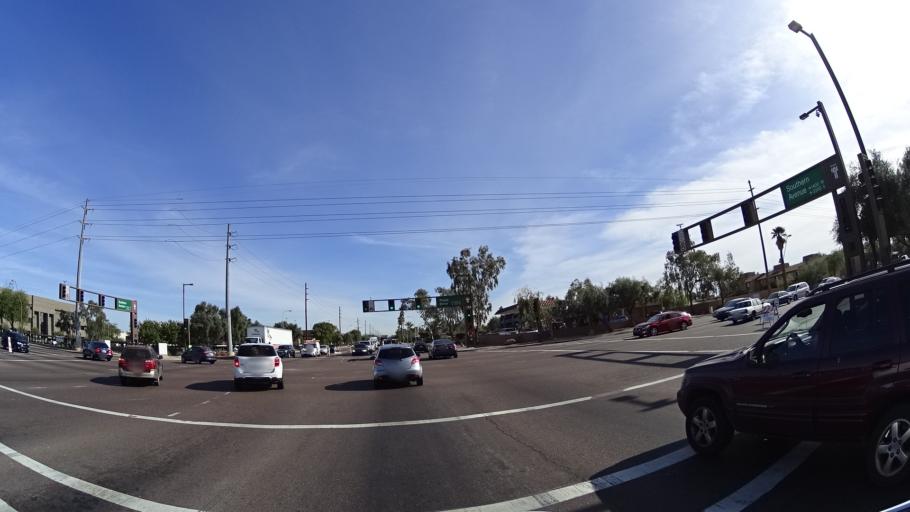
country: US
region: Arizona
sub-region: Maricopa County
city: Guadalupe
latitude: 33.3928
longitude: -111.9611
